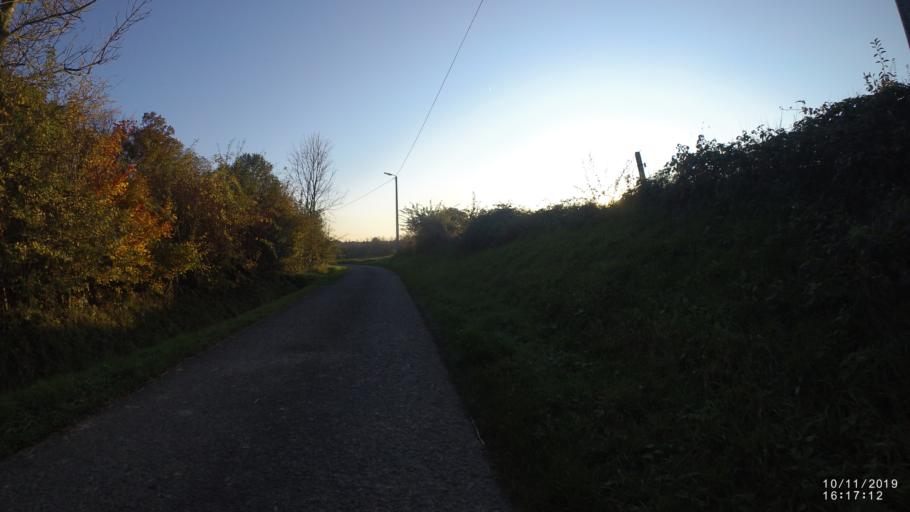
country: BE
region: Flanders
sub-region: Provincie Vlaams-Brabant
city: Lubbeek
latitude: 50.8921
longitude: 4.8503
